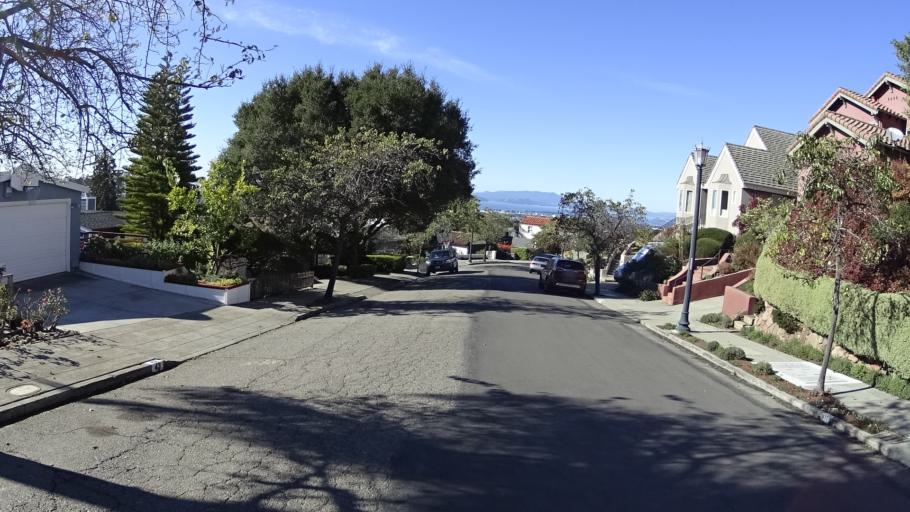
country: US
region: California
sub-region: Alameda County
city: Piedmont
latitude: 37.8408
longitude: -122.2285
